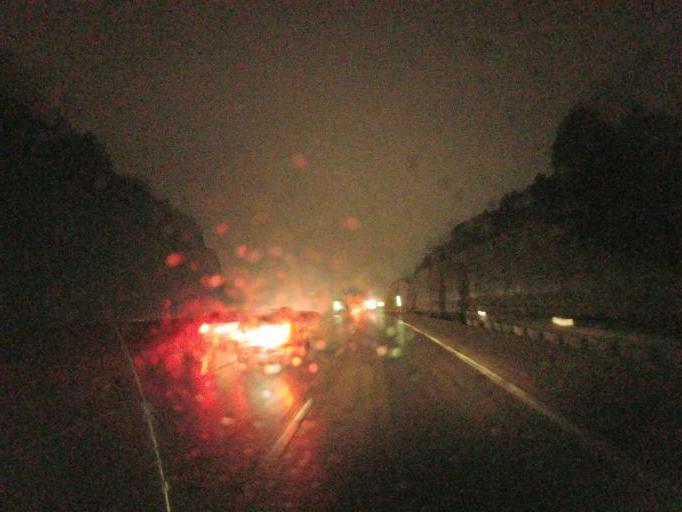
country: US
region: Missouri
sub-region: Franklin County
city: Pacific
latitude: 38.4894
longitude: -90.7454
